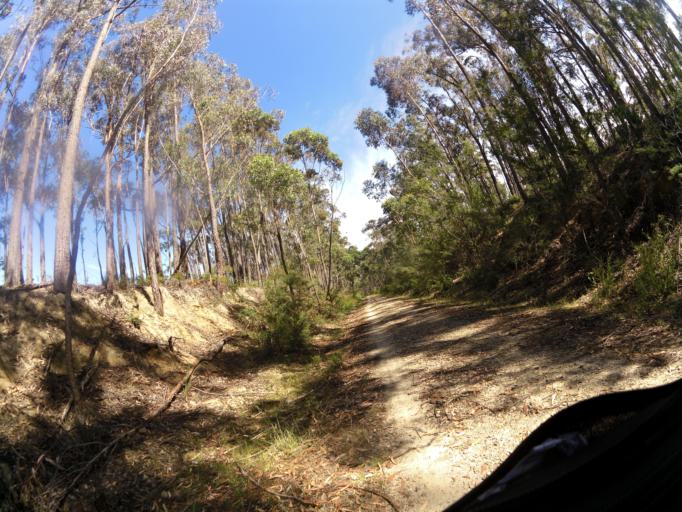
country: AU
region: Victoria
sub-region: East Gippsland
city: Lakes Entrance
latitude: -37.7218
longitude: 148.1466
